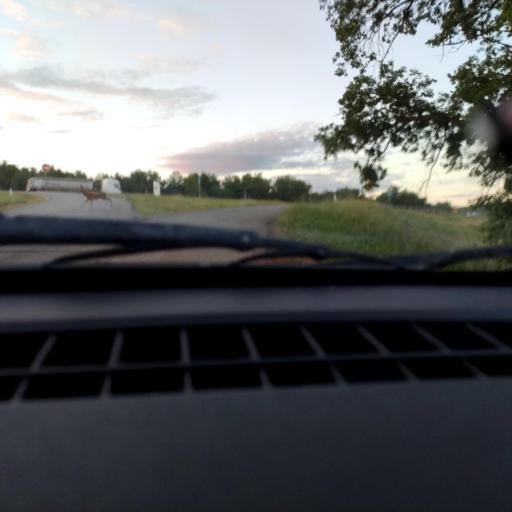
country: RU
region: Bashkortostan
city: Avdon
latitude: 54.6387
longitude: 55.5922
